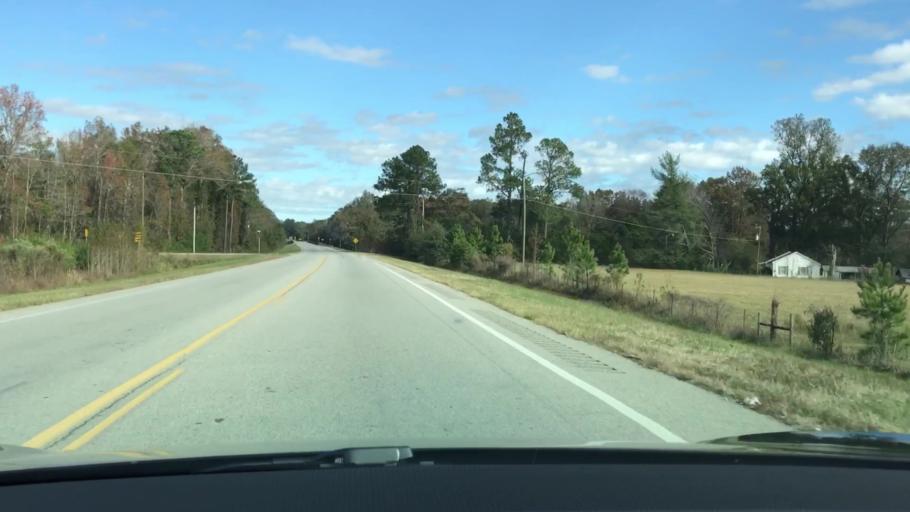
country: US
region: Georgia
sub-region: Jefferson County
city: Louisville
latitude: 32.9641
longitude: -82.3906
